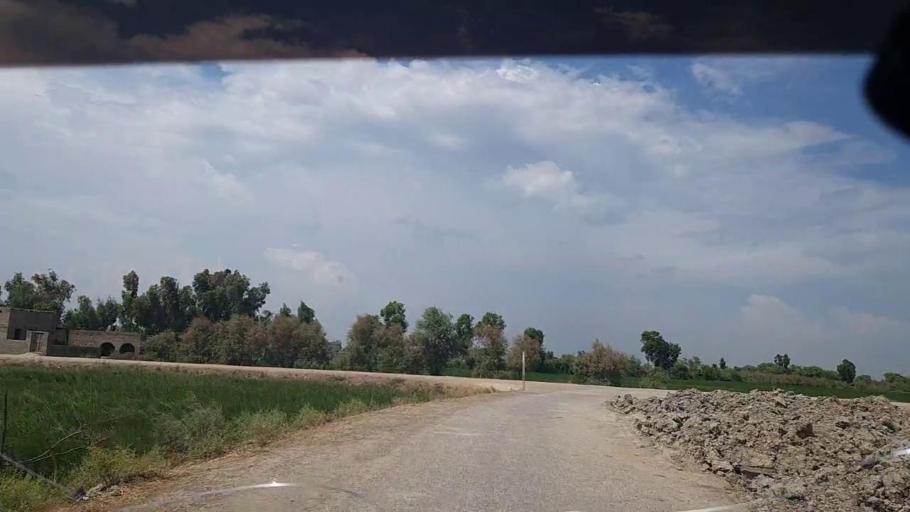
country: PK
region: Sindh
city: Ghauspur
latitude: 28.1545
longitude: 68.9971
